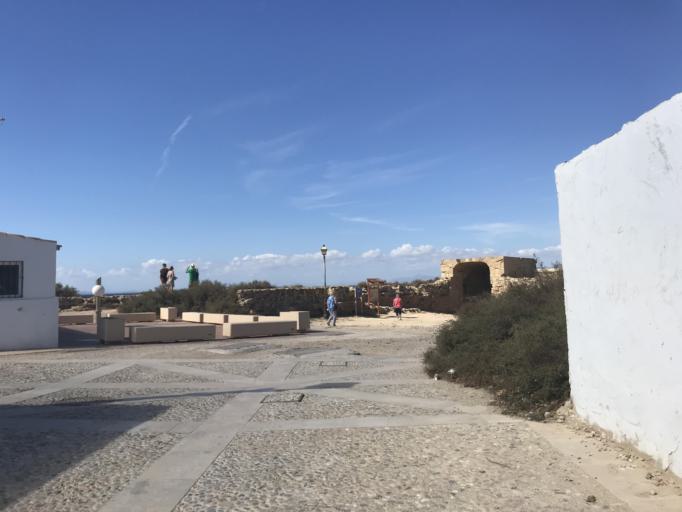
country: ES
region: Valencia
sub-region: Provincia de Alicante
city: Santa Pola
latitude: 38.1665
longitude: -0.4837
